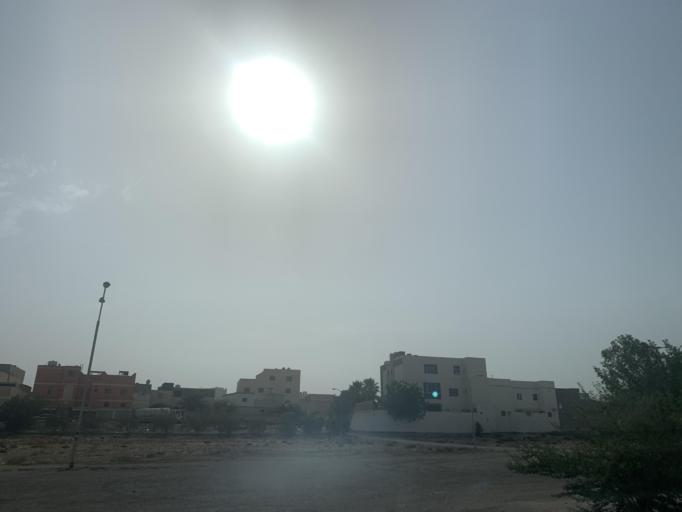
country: BH
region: Northern
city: Madinat `Isa
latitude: 26.1871
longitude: 50.4890
